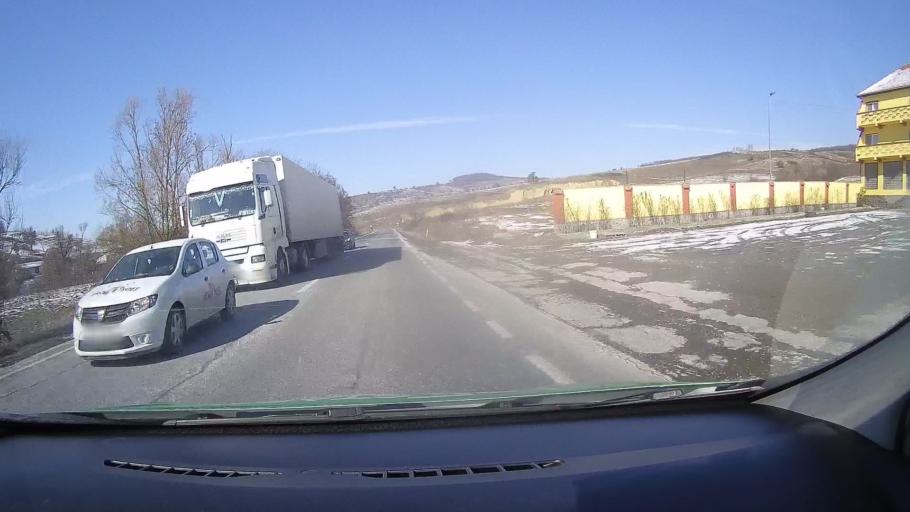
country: RO
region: Brasov
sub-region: Oras Rupea
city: Rupea
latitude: 46.0395
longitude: 25.2024
